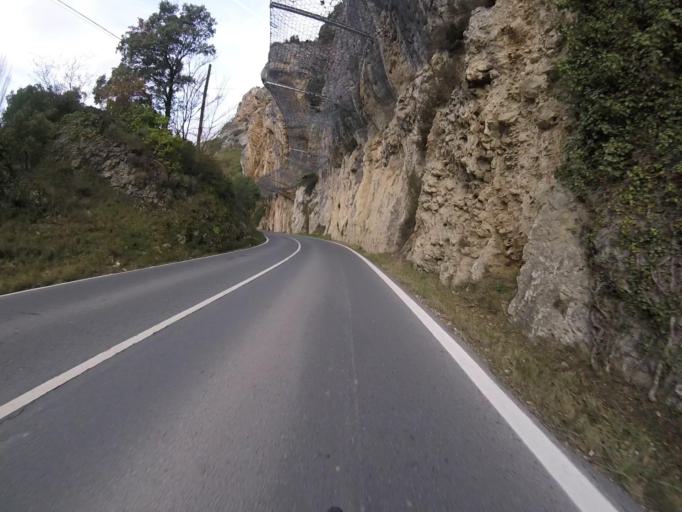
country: ES
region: Navarre
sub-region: Provincia de Navarra
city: Estella
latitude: 42.6997
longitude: -2.0564
